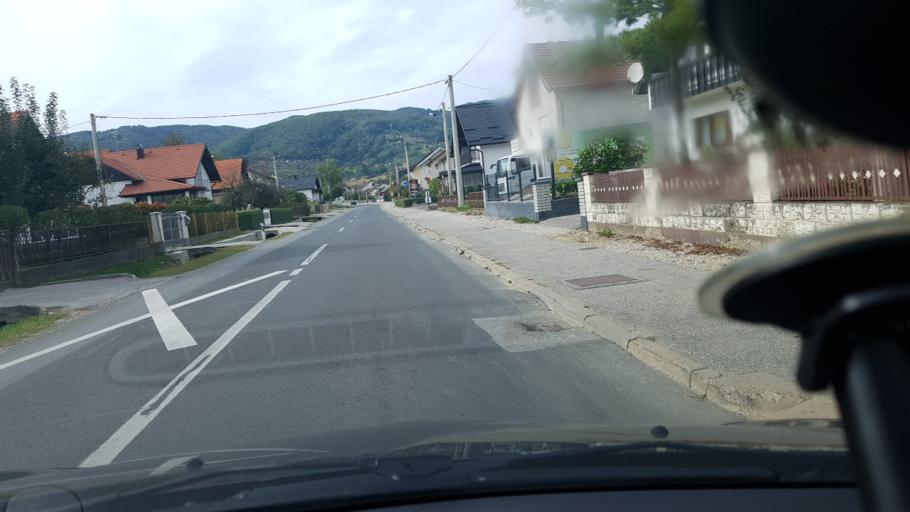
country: HR
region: Varazdinska
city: Remetinec
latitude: 46.1650
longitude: 16.3242
